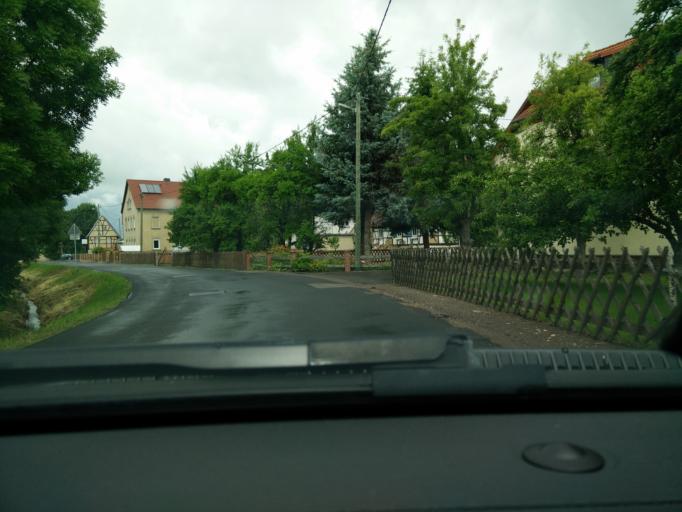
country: DE
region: Saxony
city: Geithain
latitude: 51.0898
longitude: 12.6851
